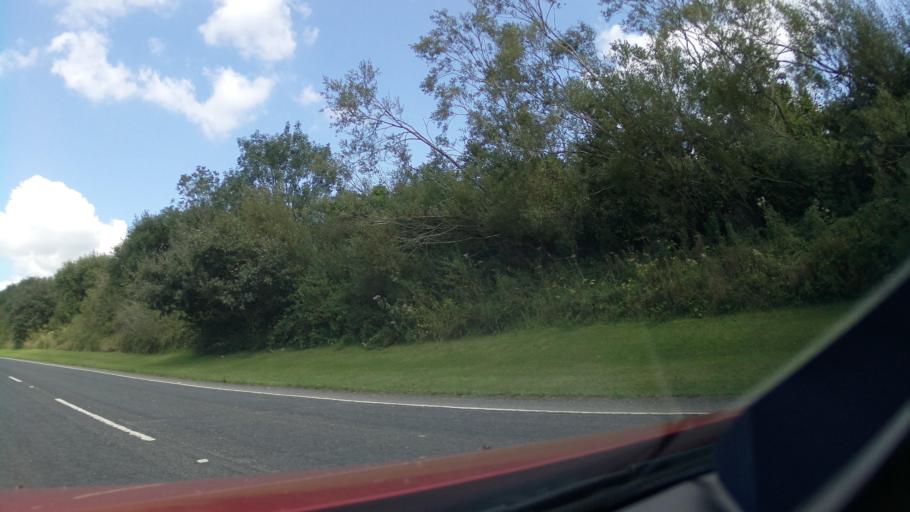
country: GB
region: England
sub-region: Cornwall
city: Saltash
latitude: 50.4333
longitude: -4.2571
